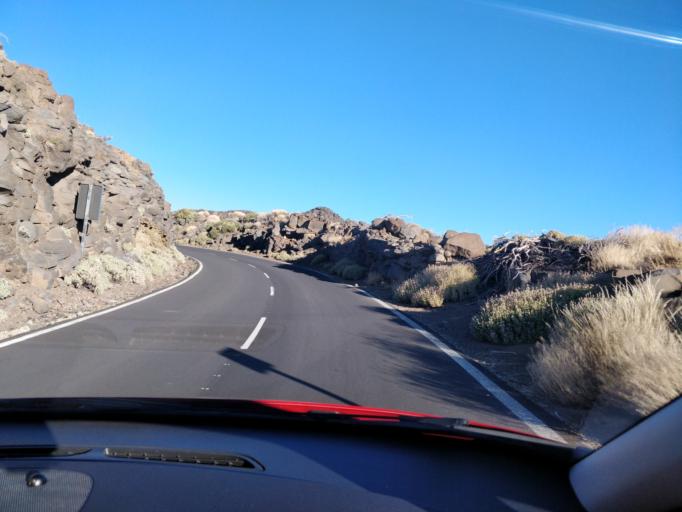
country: ES
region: Canary Islands
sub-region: Provincia de Santa Cruz de Tenerife
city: Guimar
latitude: 28.2970
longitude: -16.5111
